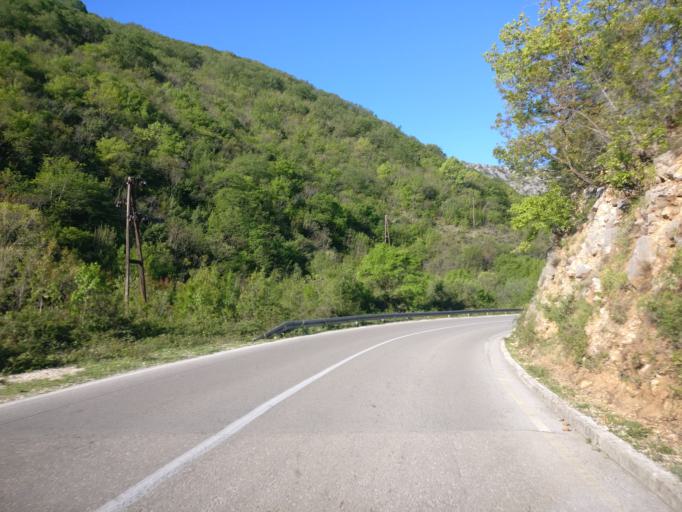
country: BA
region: Federation of Bosnia and Herzegovina
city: Stolac
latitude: 43.0719
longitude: 18.0510
